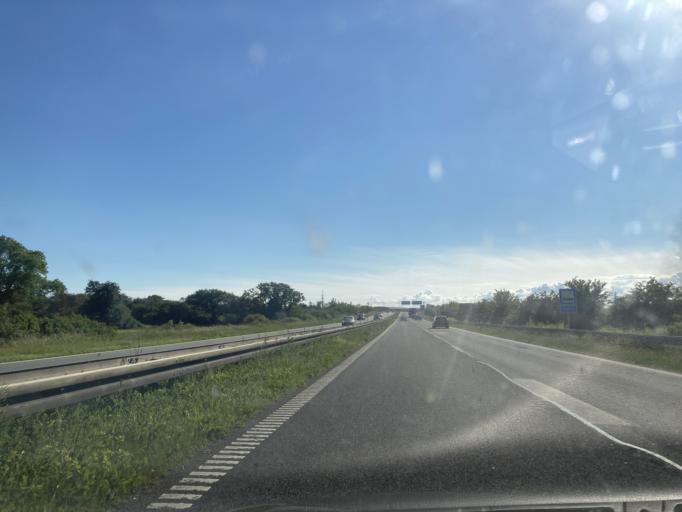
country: DK
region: Zealand
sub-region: Slagelse Kommune
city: Korsor
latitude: 55.3554
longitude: 11.1511
